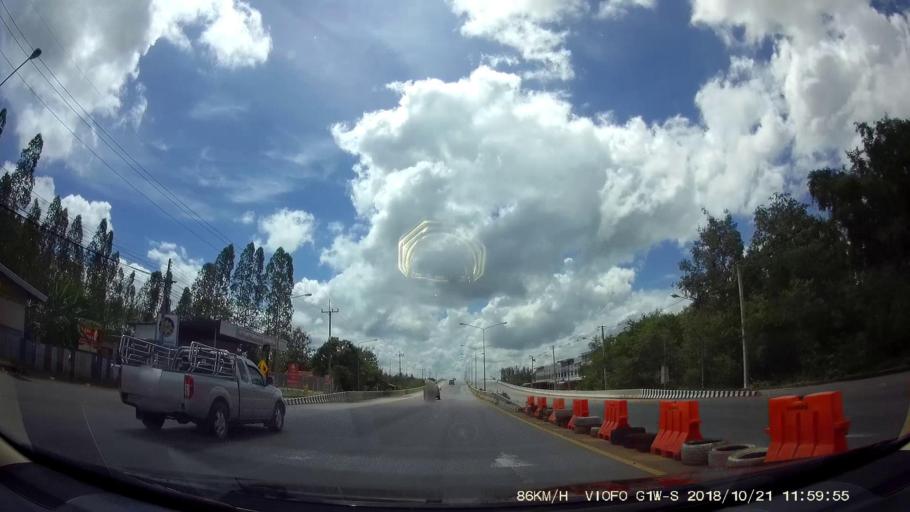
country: TH
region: Chaiyaphum
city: Chatturat
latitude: 15.5575
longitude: 101.8462
